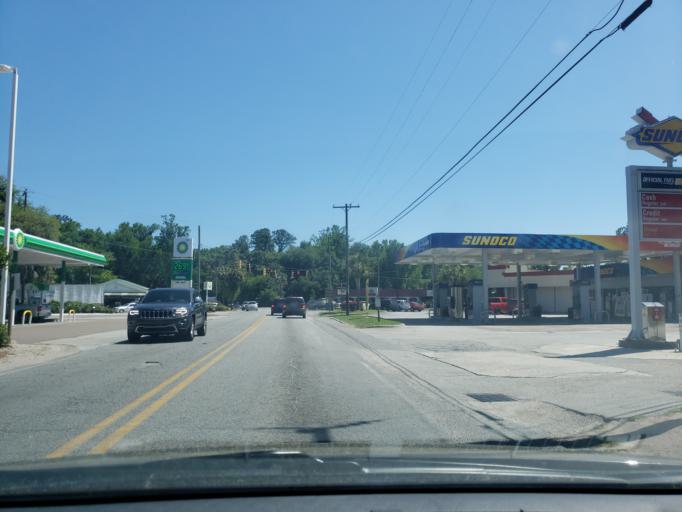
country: US
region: Georgia
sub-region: Chatham County
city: Isle of Hope
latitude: 31.9863
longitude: -81.0746
